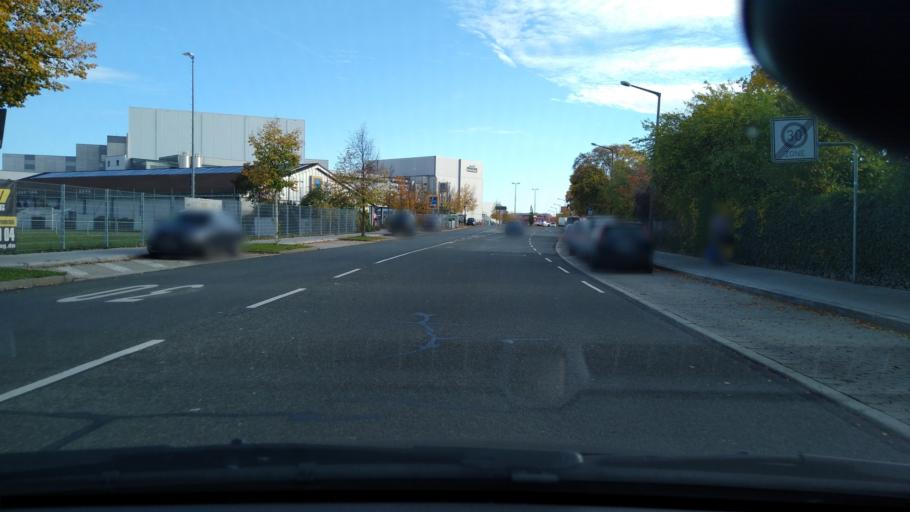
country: DE
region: Bavaria
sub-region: Regierungsbezirk Mittelfranken
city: Furth
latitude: 49.4551
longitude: 11.0006
